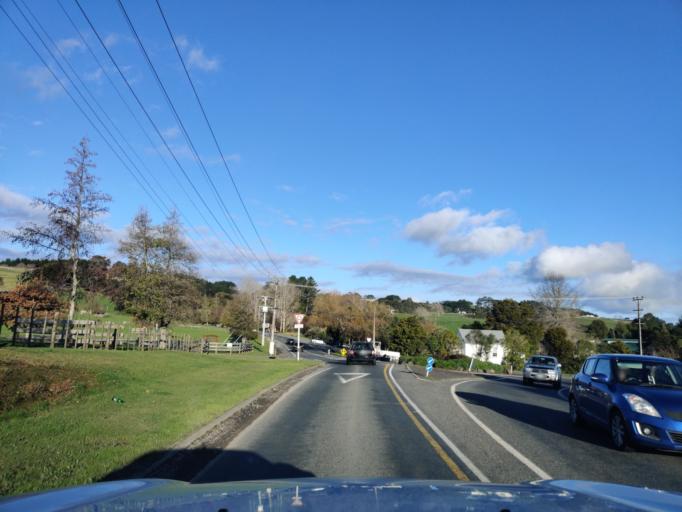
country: NZ
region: Auckland
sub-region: Auckland
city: Red Hill
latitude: -36.9864
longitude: 174.9941
